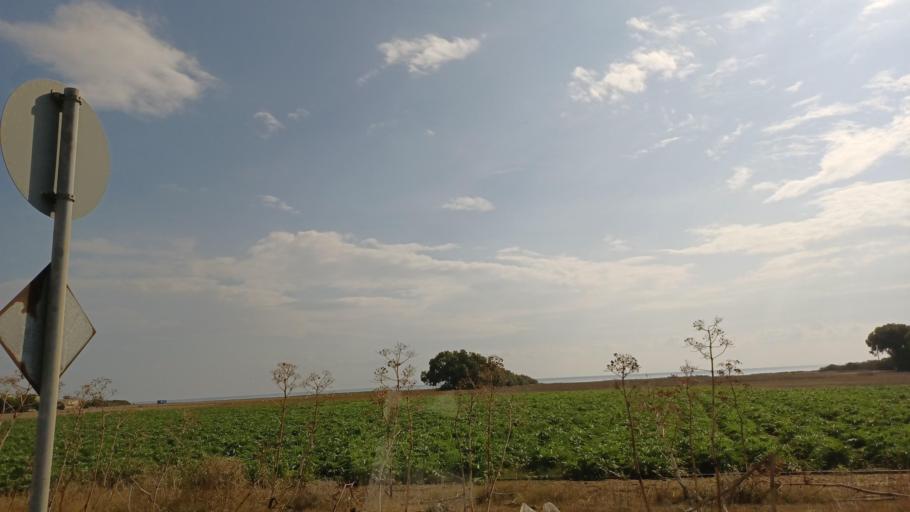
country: CY
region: Larnaka
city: Perivolia
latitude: 34.8241
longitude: 33.5693
